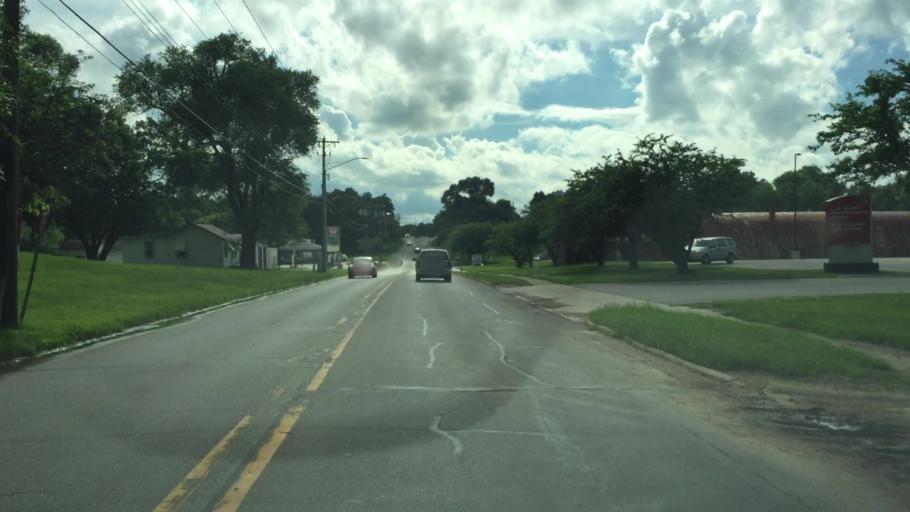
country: US
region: Iowa
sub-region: Jasper County
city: Newton
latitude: 41.6993
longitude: -93.0694
